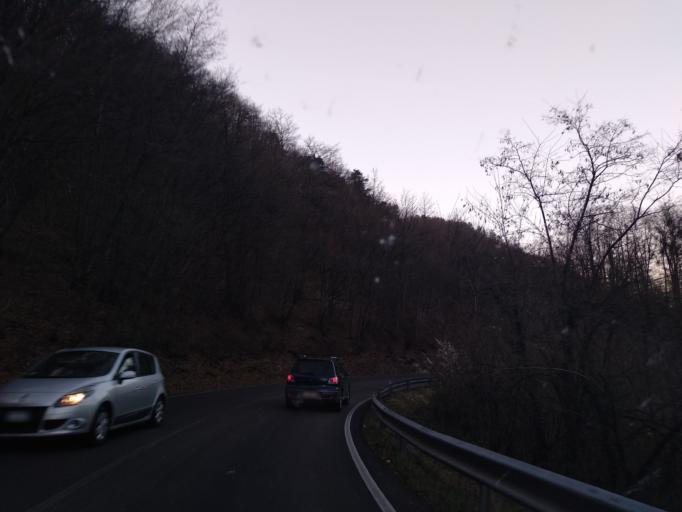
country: IT
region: Emilia-Romagna
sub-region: Provincia di Reggio Emilia
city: Casina
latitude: 44.5395
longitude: 10.5194
